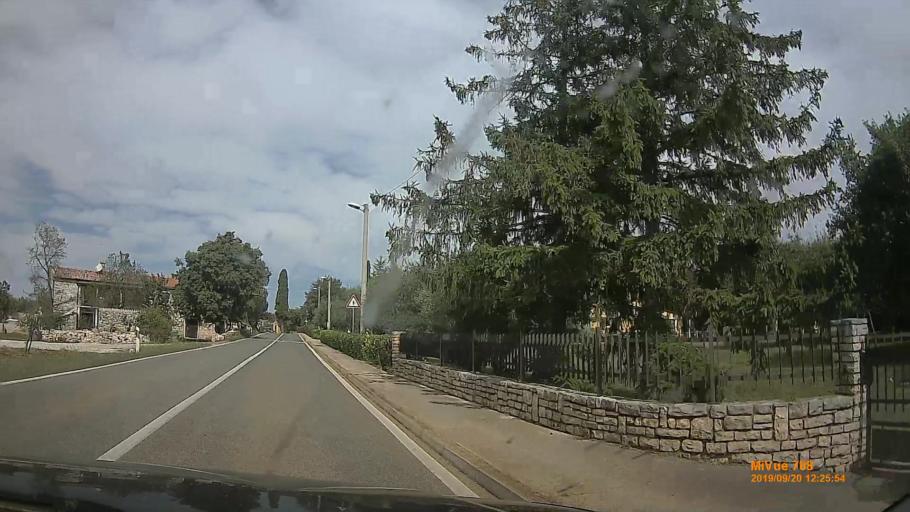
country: HR
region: Istarska
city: Umag
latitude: 45.3960
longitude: 13.5415
